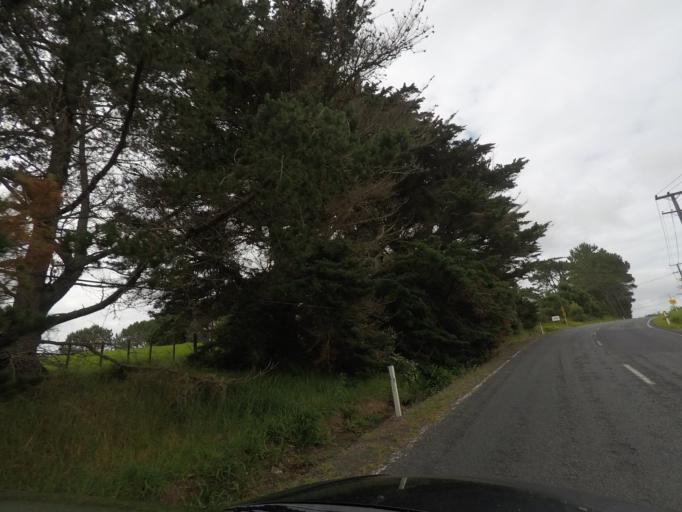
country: NZ
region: Auckland
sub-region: Auckland
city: Rosebank
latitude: -36.8297
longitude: 174.5755
